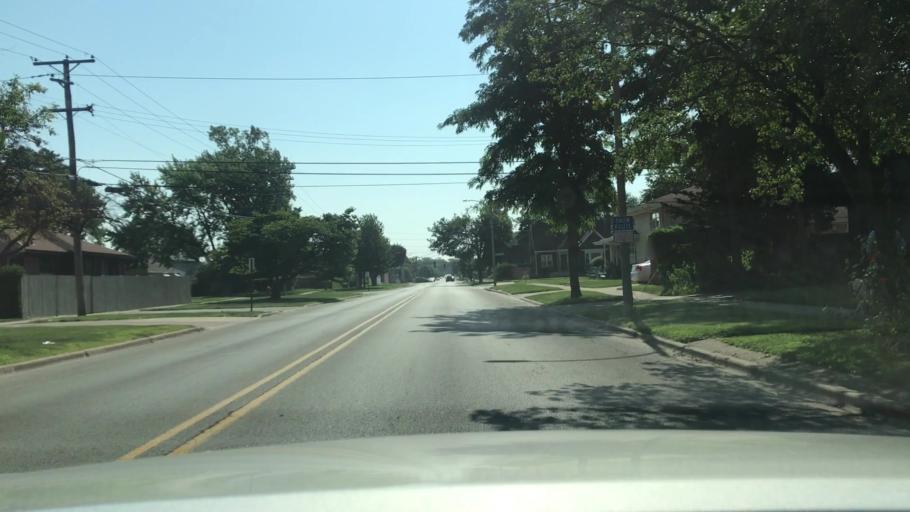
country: US
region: Illinois
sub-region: Cook County
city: Evergreen Park
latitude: 41.7134
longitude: -87.7051
